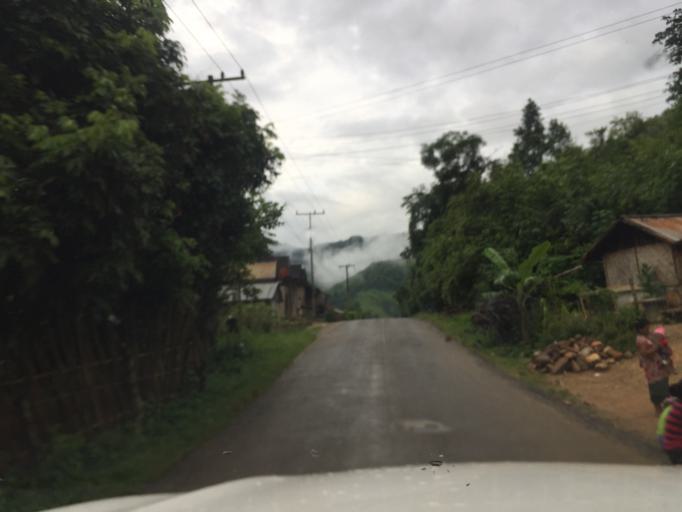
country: LA
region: Oudomxai
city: Muang La
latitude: 20.8947
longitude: 102.1790
